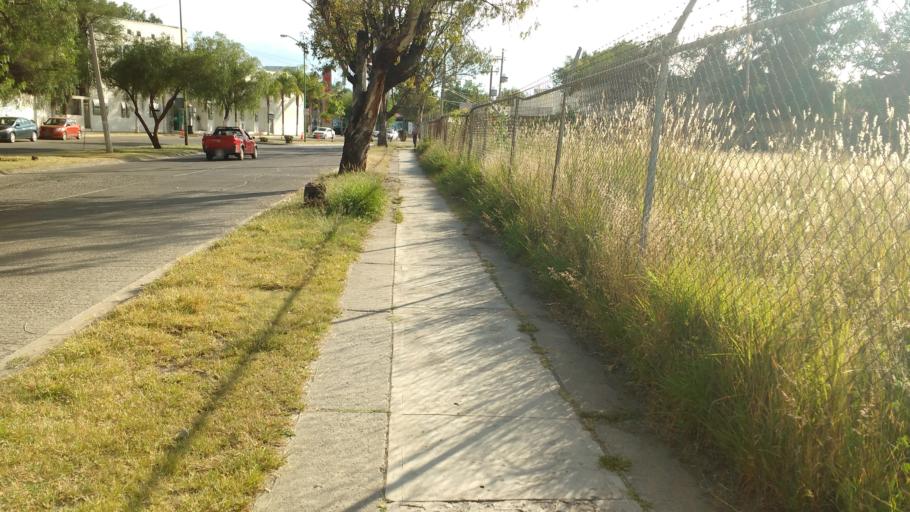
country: MX
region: Guanajuato
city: Leon
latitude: 21.1063
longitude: -101.6438
